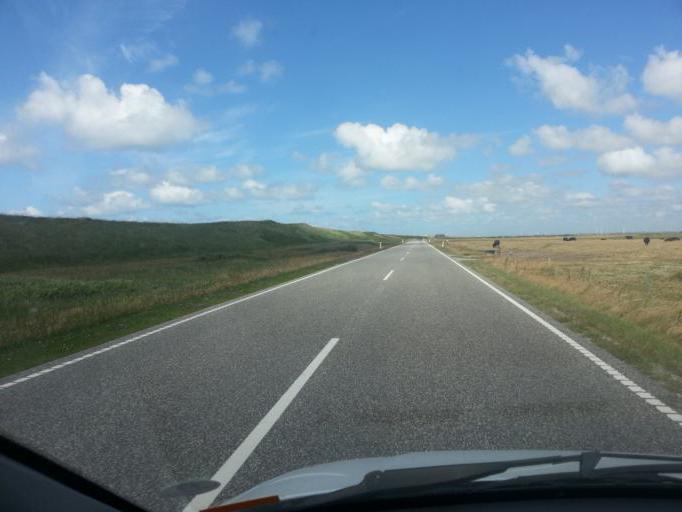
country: DK
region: Central Jutland
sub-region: Holstebro Kommune
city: Ulfborg
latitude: 56.3886
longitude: 8.1217
